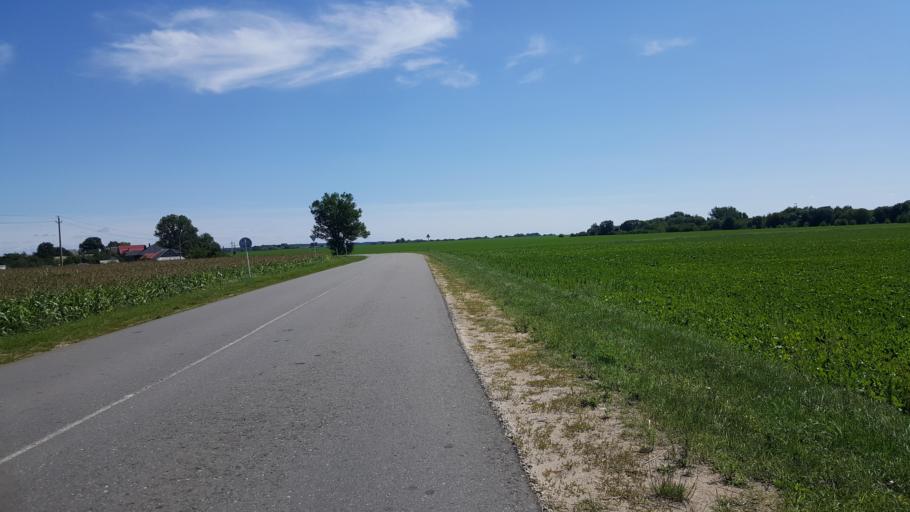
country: BY
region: Brest
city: Charnawchytsy
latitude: 52.2202
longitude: 23.7519
